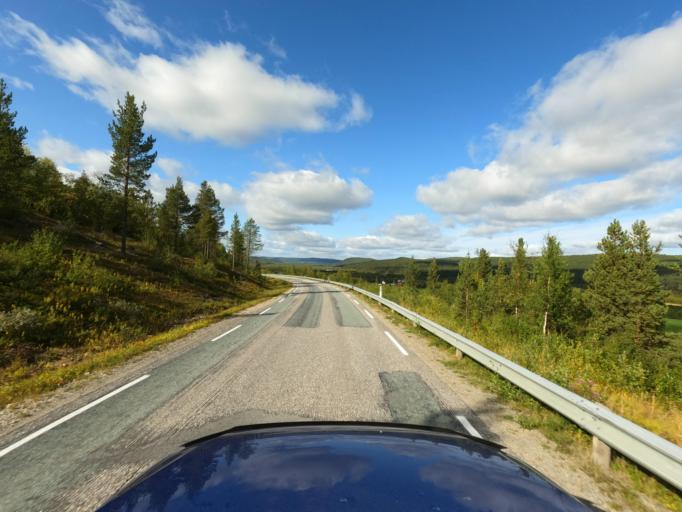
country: NO
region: Finnmark Fylke
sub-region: Karasjok
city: Karasjohka
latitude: 69.4348
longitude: 25.7104
